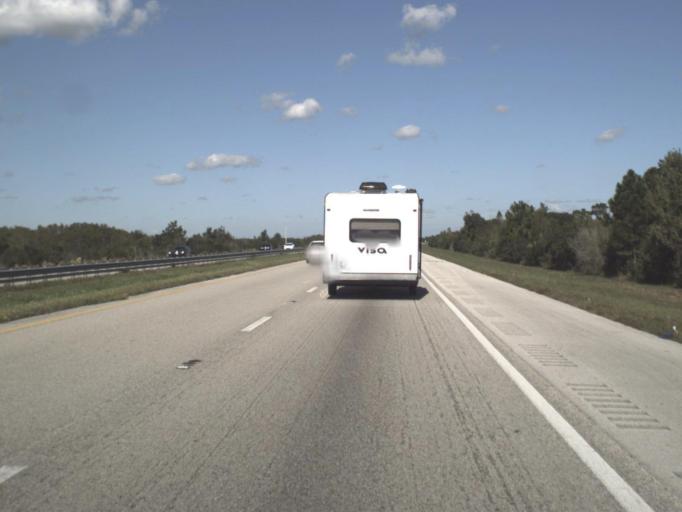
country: US
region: Florida
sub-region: Brevard County
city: June Park
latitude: 27.8851
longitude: -81.0314
